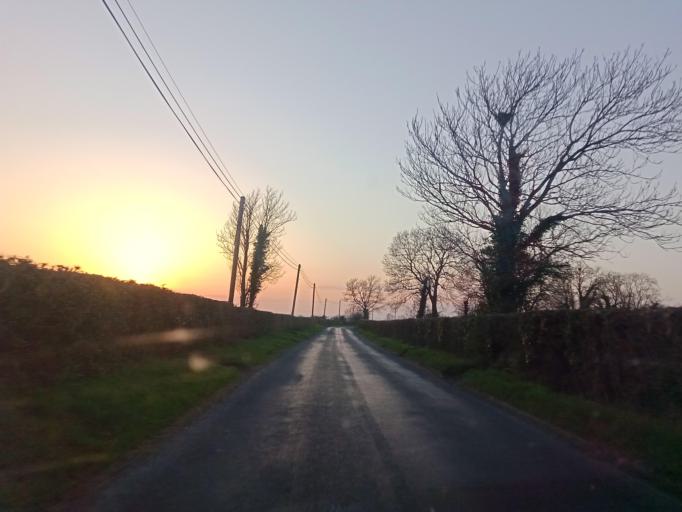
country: IE
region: Leinster
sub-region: Laois
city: Abbeyleix
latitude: 52.9495
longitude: -7.3502
